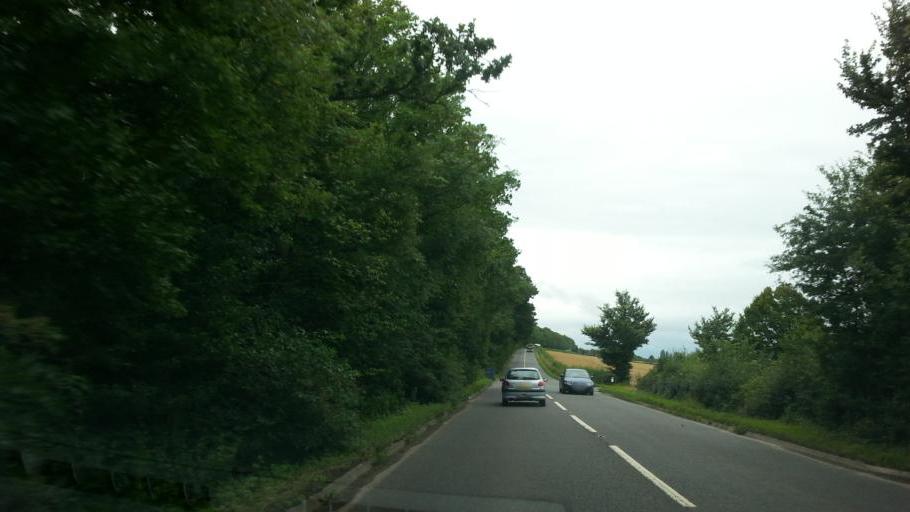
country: GB
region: England
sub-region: Wiltshire
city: North Bradley
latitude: 51.3091
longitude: -2.1720
